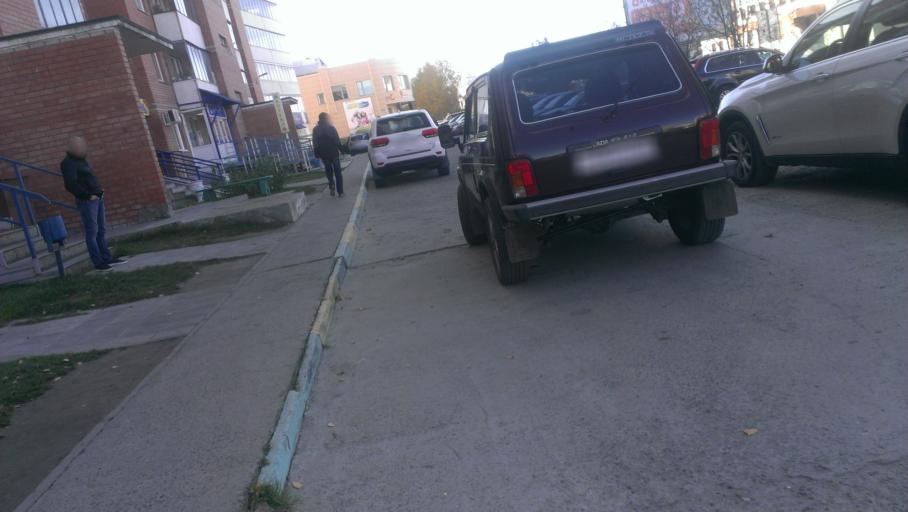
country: RU
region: Altai Krai
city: Novosilikatnyy
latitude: 53.3344
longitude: 83.6835
